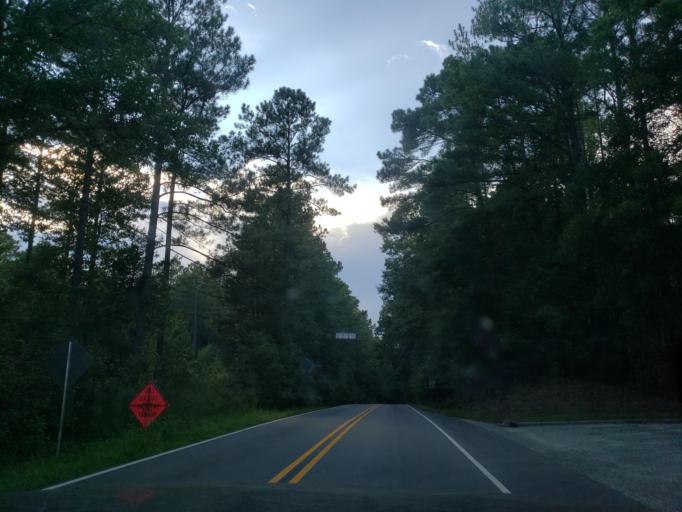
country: US
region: North Carolina
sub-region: Durham County
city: Durham
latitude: 35.9900
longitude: -78.9687
